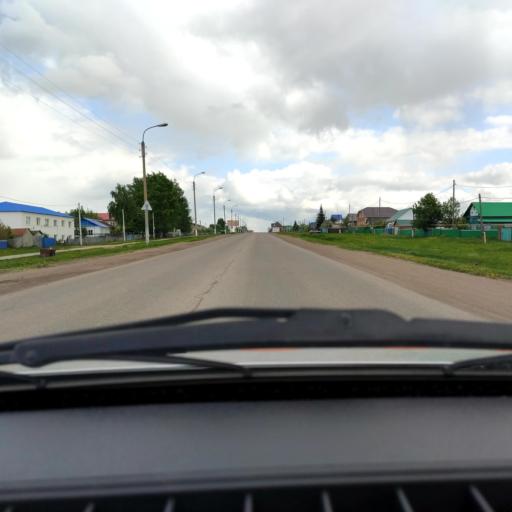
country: RU
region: Bashkortostan
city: Tolbazy
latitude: 53.9981
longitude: 55.9016
